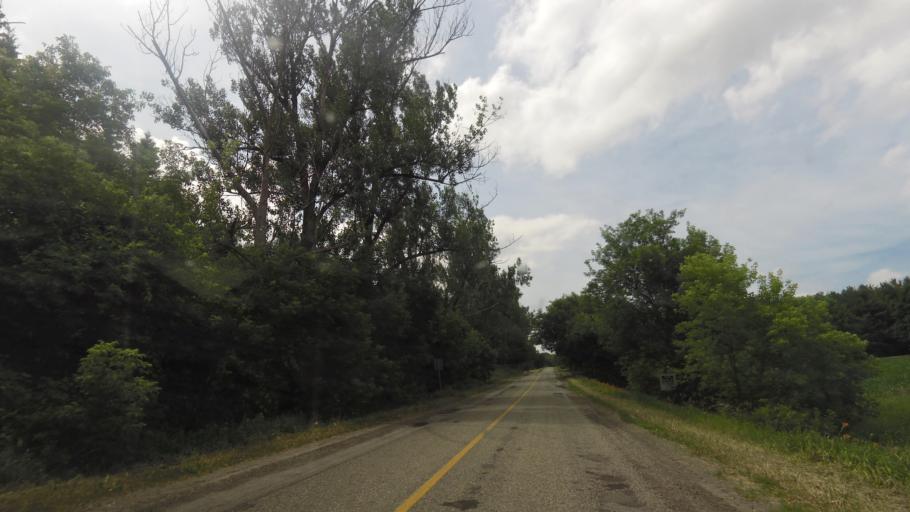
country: CA
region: Ontario
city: Orangeville
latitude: 43.8640
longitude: -79.9052
